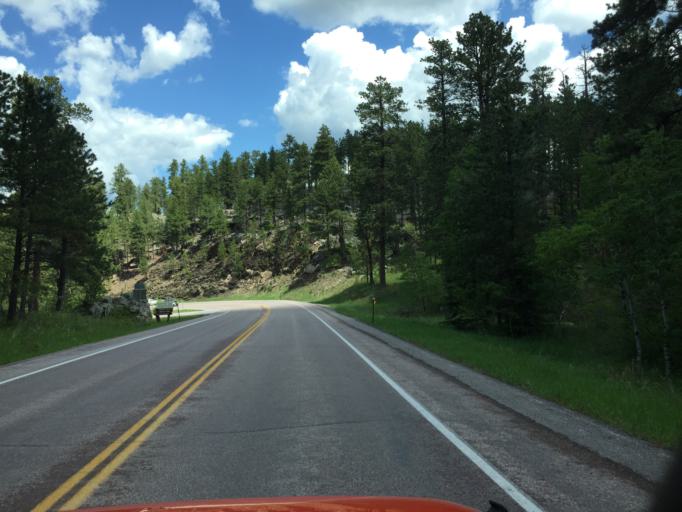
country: US
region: South Dakota
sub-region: Custer County
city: Custer
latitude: 43.8895
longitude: -103.4791
